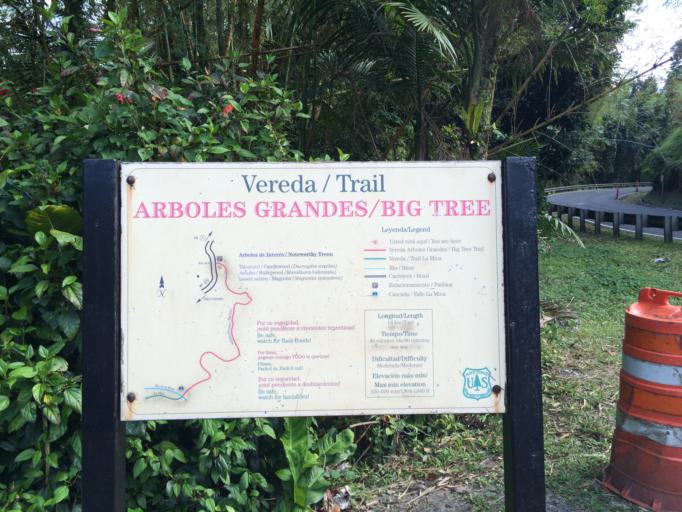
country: PR
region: Rio Grande
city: Palmer
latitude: 18.3085
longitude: -65.7751
